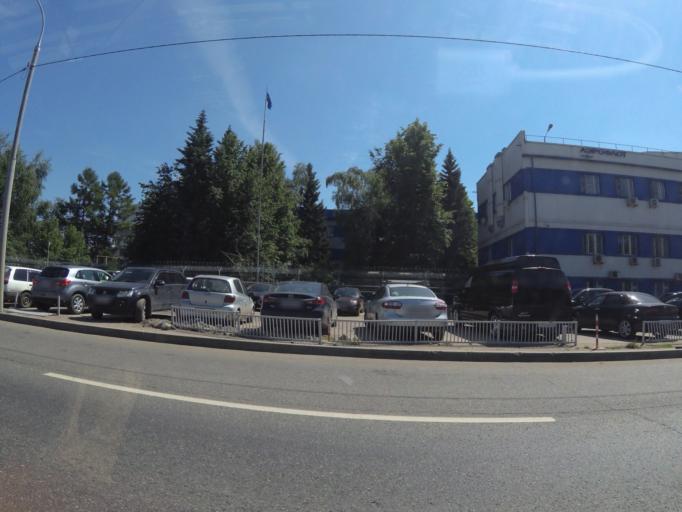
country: RU
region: Moskovskaya
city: Novopodrezkovo
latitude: 55.9800
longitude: 37.3999
